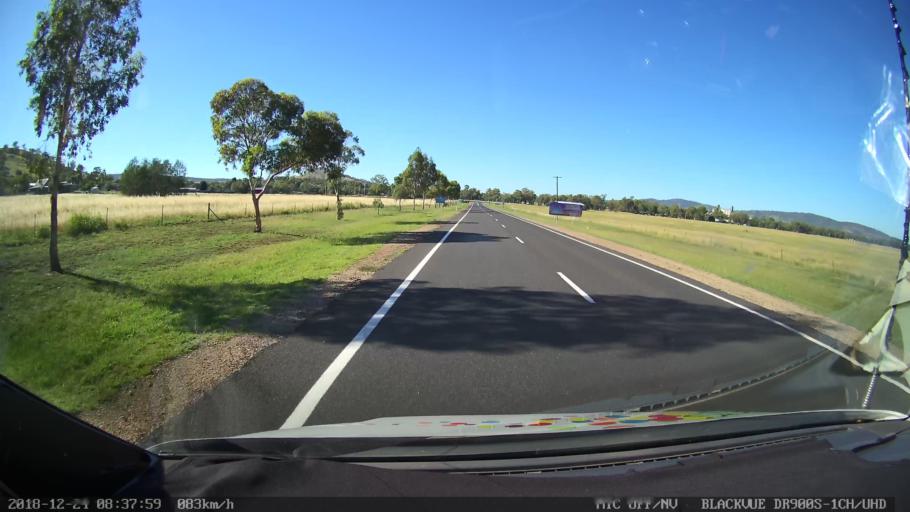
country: AU
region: New South Wales
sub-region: Liverpool Plains
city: Quirindi
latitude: -31.3364
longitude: 150.6479
